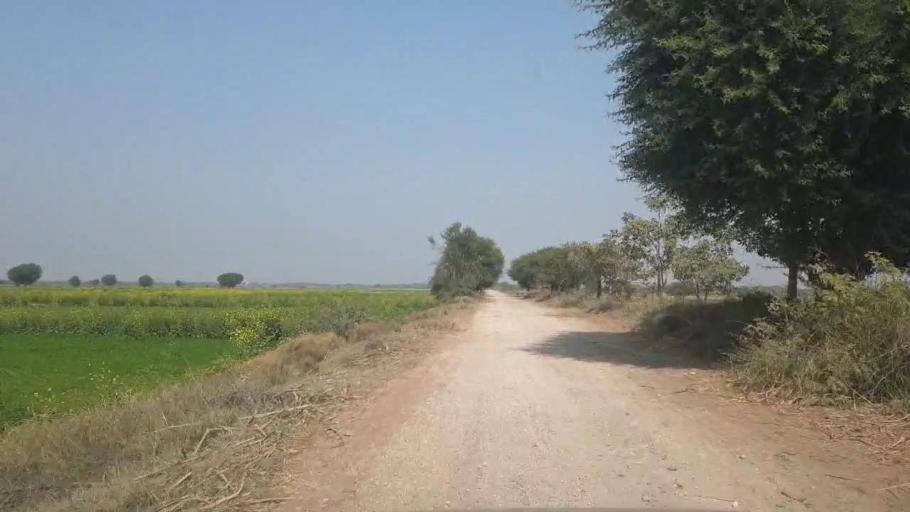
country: PK
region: Sindh
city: Tando Allahyar
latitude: 25.4571
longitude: 68.8319
